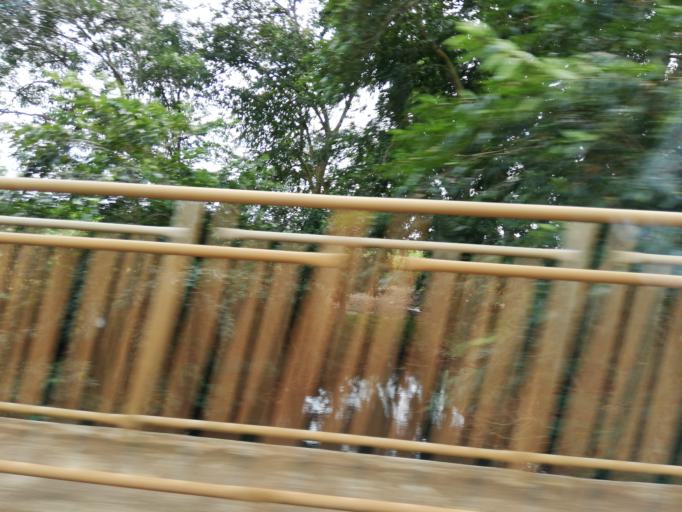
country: MU
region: Pamplemousses
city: Calebasses
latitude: -20.1017
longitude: 57.5480
